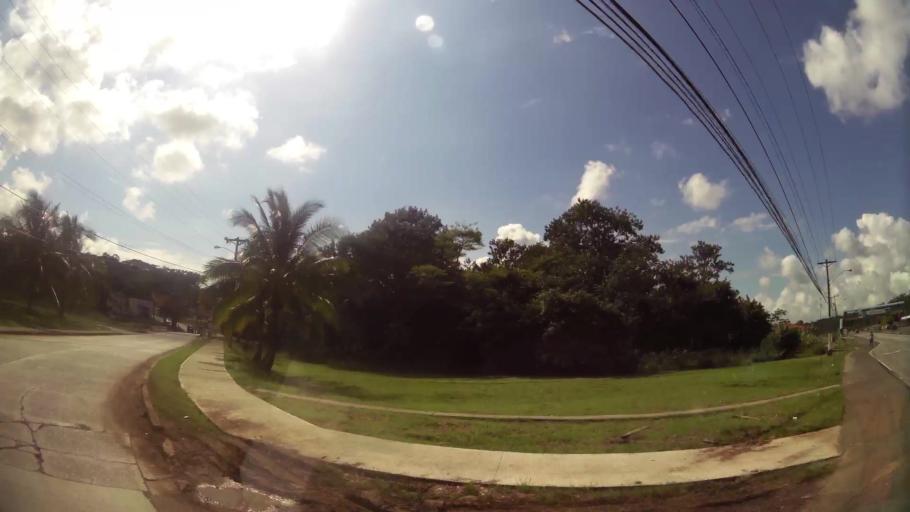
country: PA
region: Panama
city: Nuevo Arraijan
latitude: 8.9162
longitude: -79.7417
